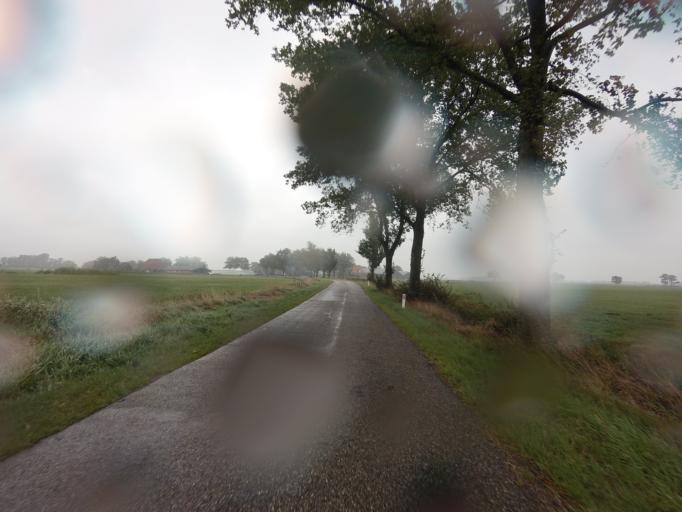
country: NL
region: Friesland
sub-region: Gemeente Boarnsterhim
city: Aldeboarn
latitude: 53.0692
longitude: 5.9271
